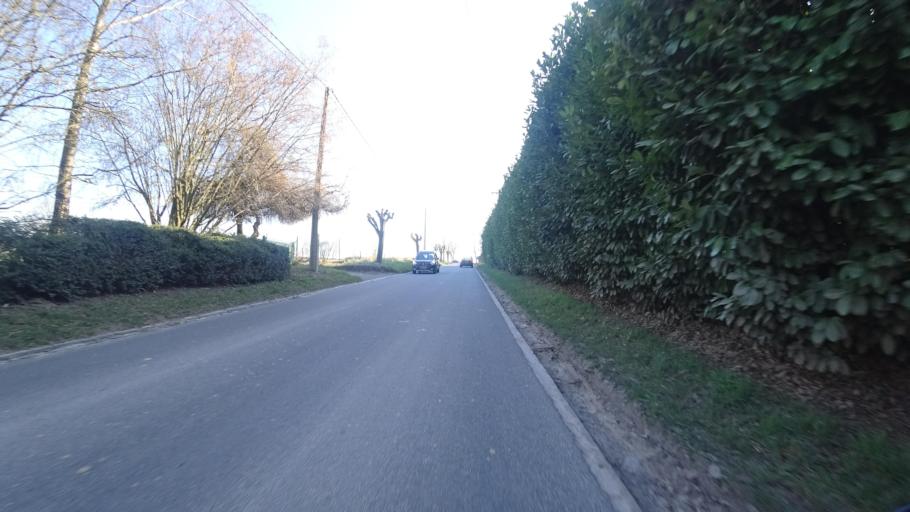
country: BE
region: Wallonia
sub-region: Province de Namur
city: Gembloux
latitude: 50.5656
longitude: 4.6687
